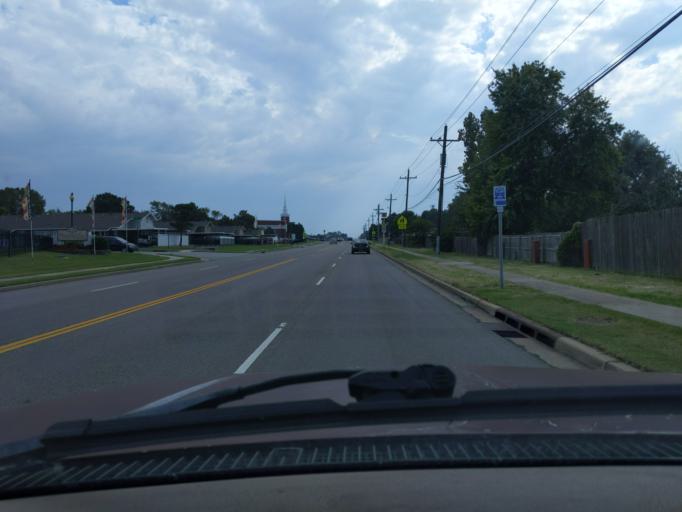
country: US
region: Oklahoma
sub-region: Tulsa County
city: Broken Arrow
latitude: 36.1388
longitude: -95.8333
